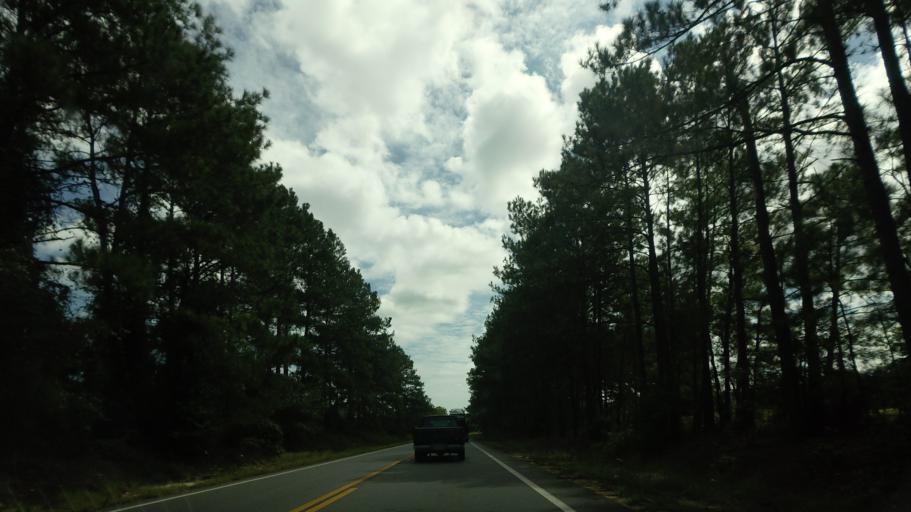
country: US
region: Georgia
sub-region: Houston County
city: Robins Air Force Base
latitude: 32.5434
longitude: -83.5583
